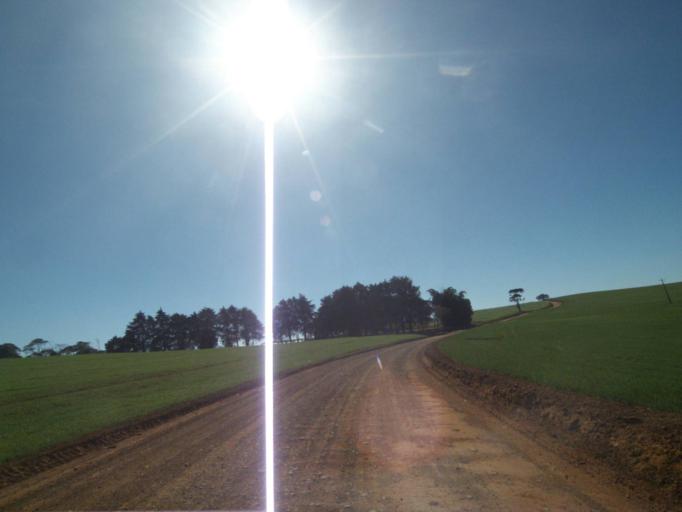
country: BR
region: Parana
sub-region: Tibagi
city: Tibagi
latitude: -24.6094
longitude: -50.6060
